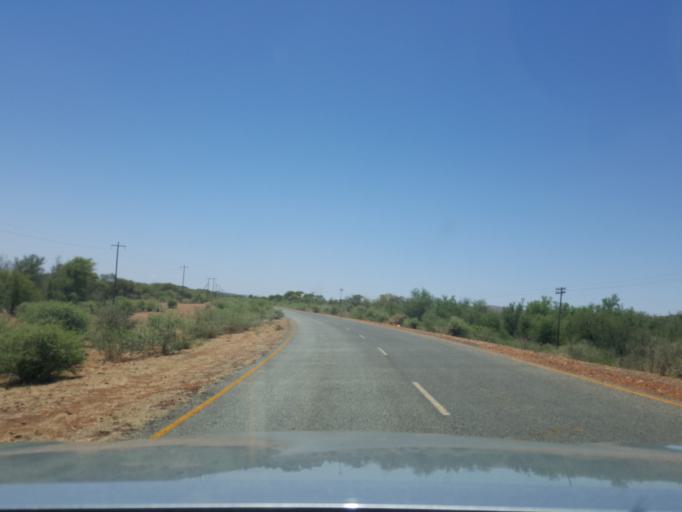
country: BW
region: South East
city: Ramotswa
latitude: -24.8838
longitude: 25.8908
